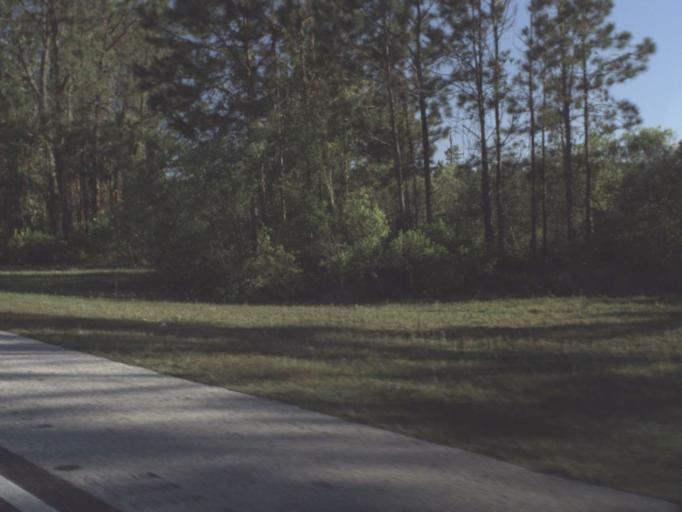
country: US
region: Florida
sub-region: Flagler County
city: Palm Coast
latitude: 29.6370
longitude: -81.2686
